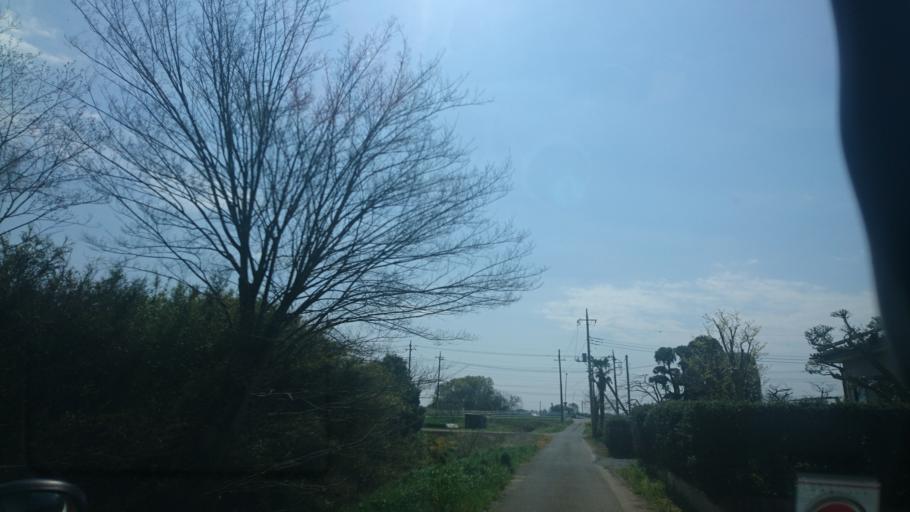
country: JP
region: Ibaraki
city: Yuki
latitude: 36.2188
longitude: 139.9194
